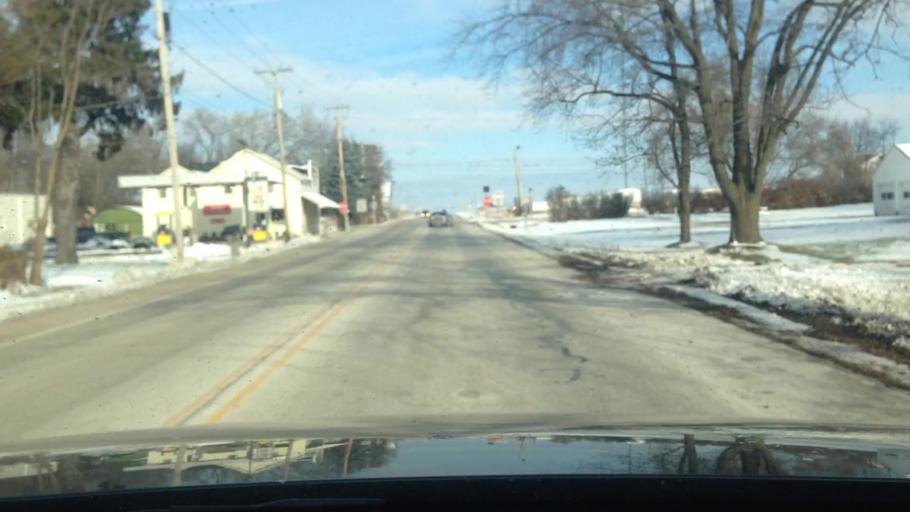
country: US
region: Wisconsin
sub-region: Walworth County
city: East Troy
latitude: 42.6903
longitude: -88.4047
